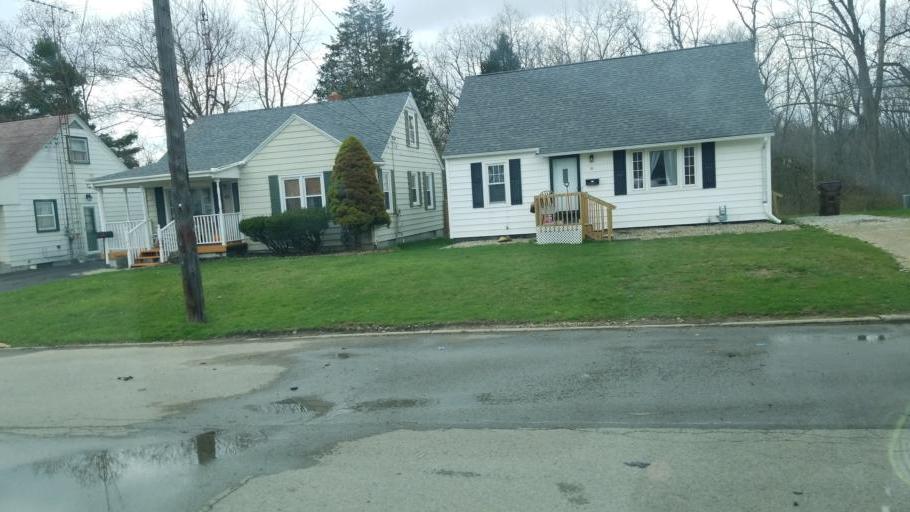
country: US
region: Ohio
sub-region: Richland County
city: Ontario
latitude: 40.7606
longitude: -82.5529
